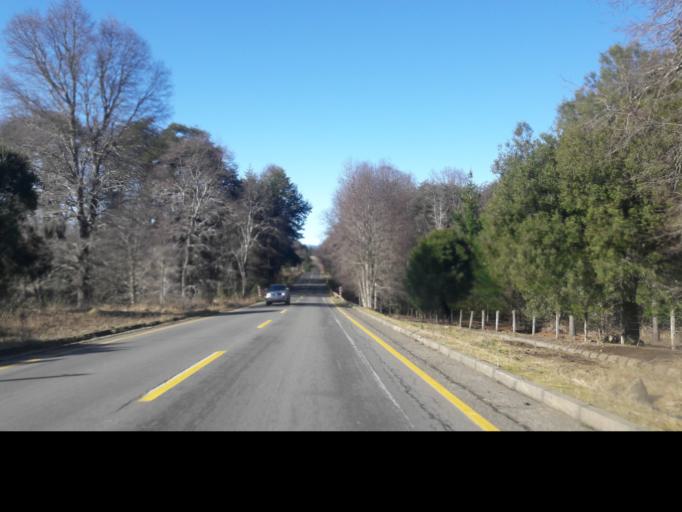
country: CL
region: Araucania
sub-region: Provincia de Malleco
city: Victoria
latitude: -38.3306
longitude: -71.9810
